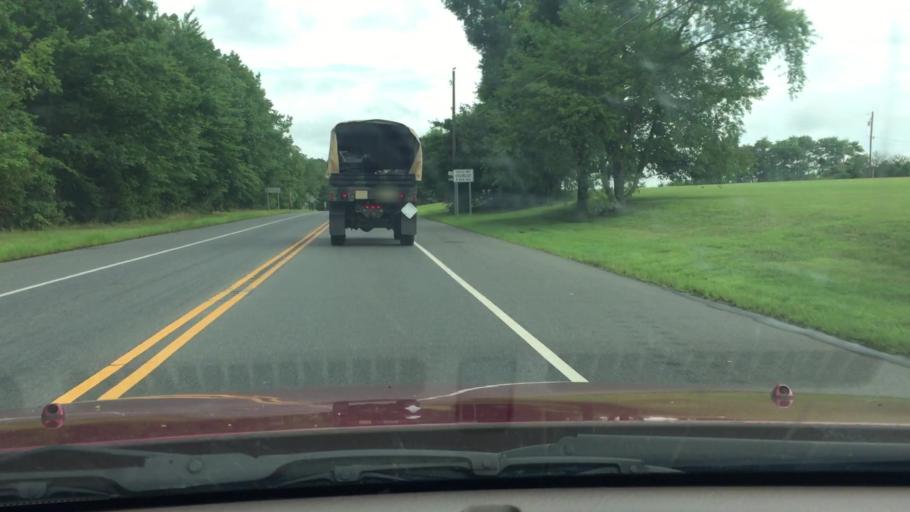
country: US
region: New Jersey
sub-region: Burlington County
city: Fort Dix
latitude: 40.0570
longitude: -74.6501
